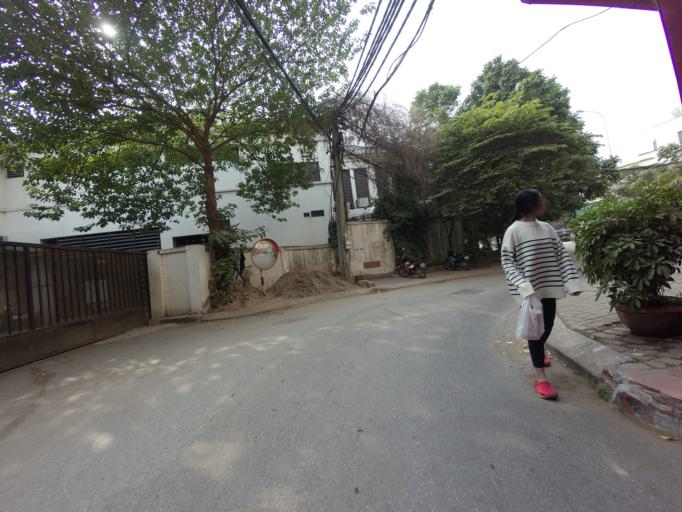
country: VN
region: Ha Noi
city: Tay Ho
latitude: 21.0590
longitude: 105.8316
